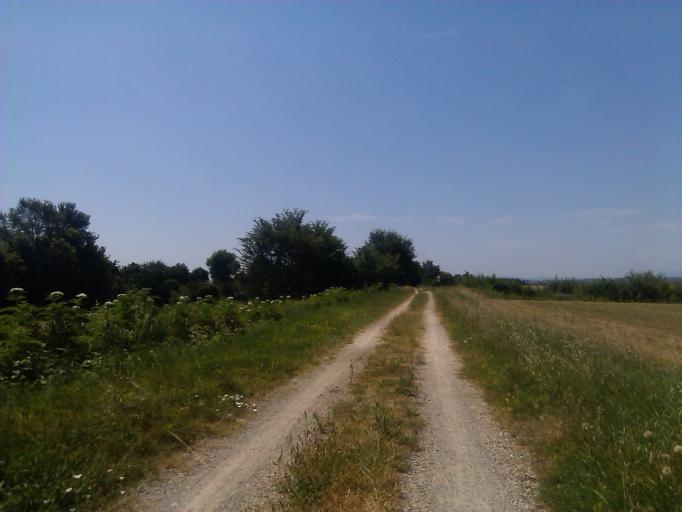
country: IT
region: Tuscany
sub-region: Province of Arezzo
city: Cesa
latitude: 43.3601
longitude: 11.8265
